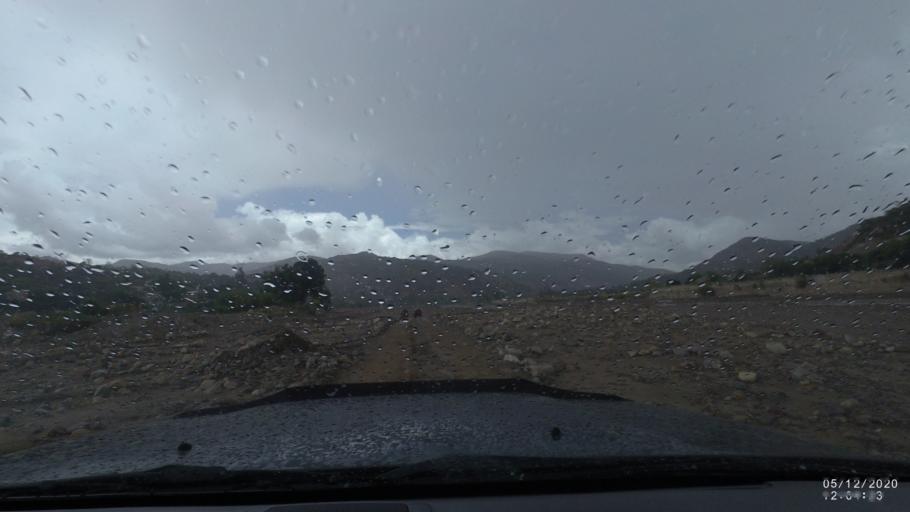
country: BO
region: Cochabamba
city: Sipe Sipe
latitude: -17.5715
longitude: -66.3564
